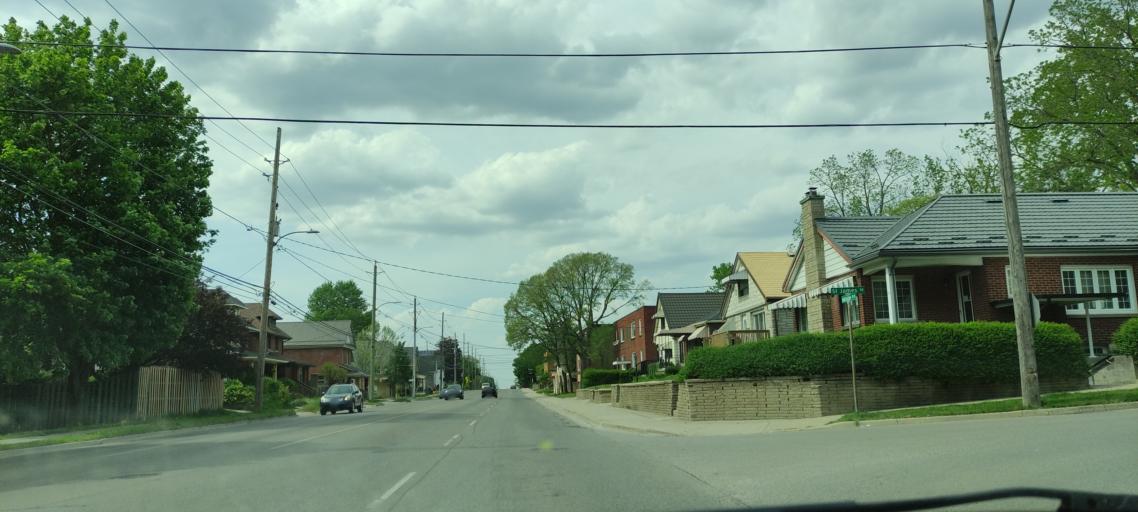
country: CA
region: Ontario
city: London
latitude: 43.0020
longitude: -81.2381
